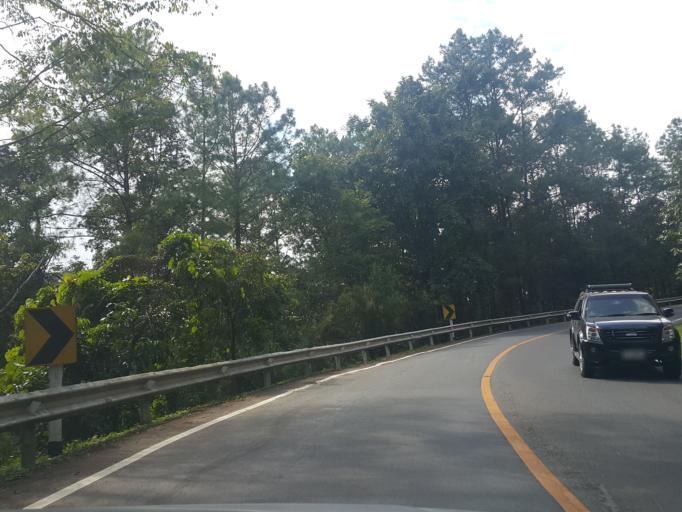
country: TH
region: Chiang Mai
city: Chom Thong
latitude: 18.5392
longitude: 98.5711
